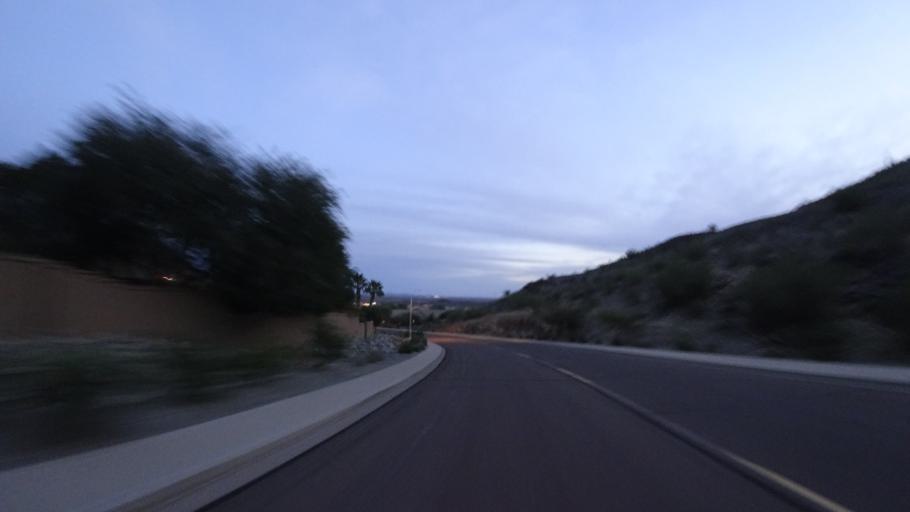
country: US
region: Arizona
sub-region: Maricopa County
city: Laveen
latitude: 33.3013
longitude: -112.0703
